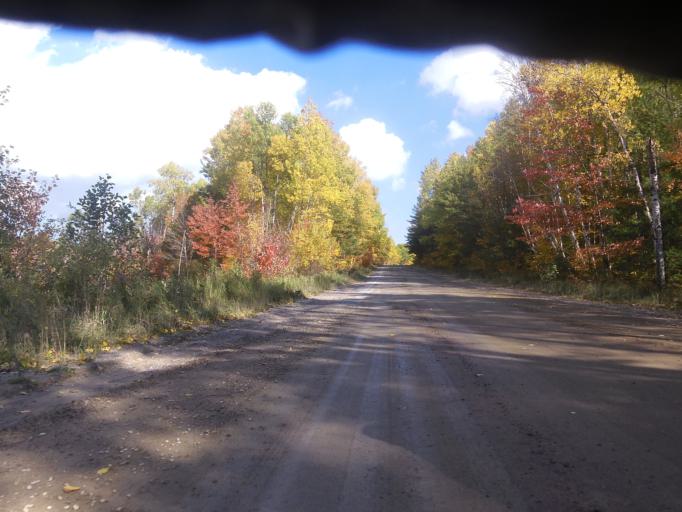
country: CA
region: Ontario
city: Petawawa
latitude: 45.8176
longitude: -77.4209
